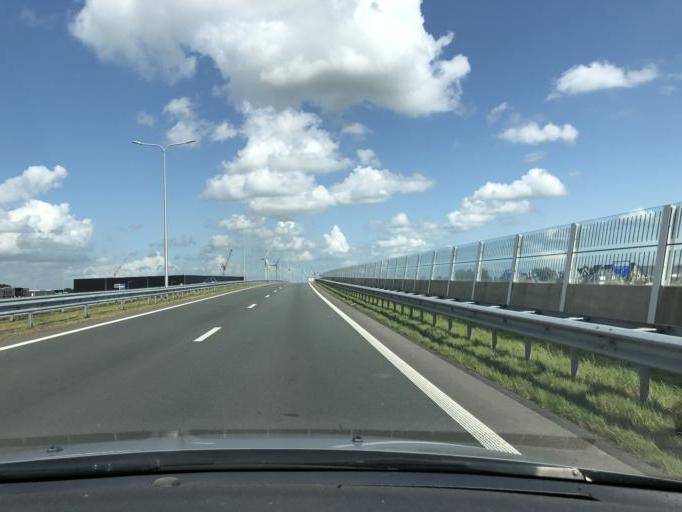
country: NL
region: North Holland
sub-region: Gemeente Hoorn
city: Hoorn
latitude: 52.6777
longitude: 5.0815
